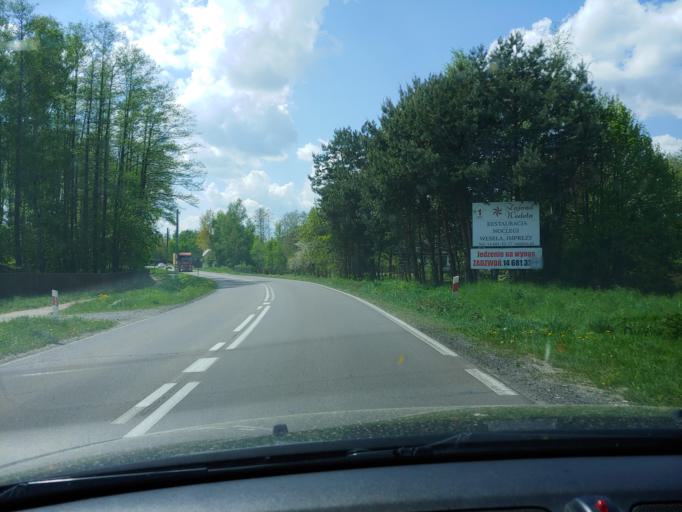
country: PL
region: Subcarpathian Voivodeship
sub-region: Powiat mielecki
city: Wadowice Gorne
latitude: 50.2578
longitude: 21.3271
